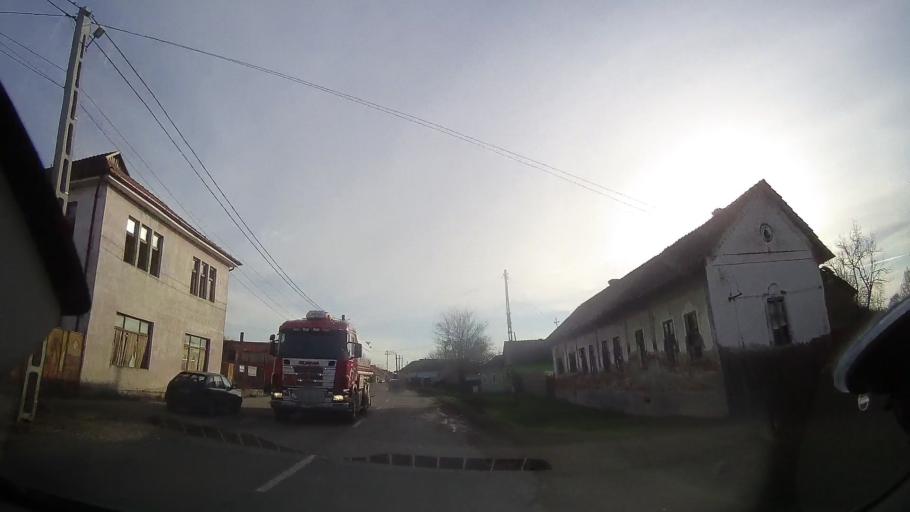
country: RO
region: Bihor
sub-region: Comuna Tileagd
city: Tileagd
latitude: 47.0704
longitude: 22.2000
